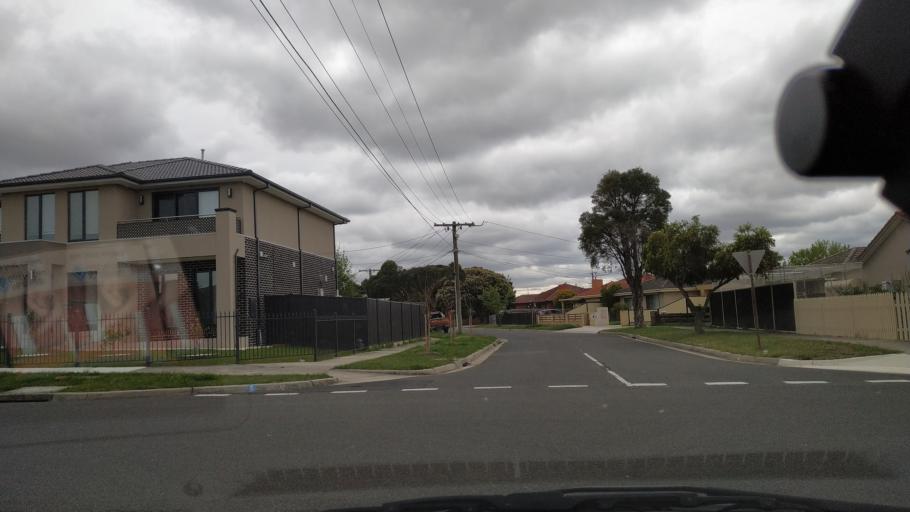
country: AU
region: Victoria
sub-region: Greater Dandenong
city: Dandenong North
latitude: -37.9625
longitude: 145.2050
